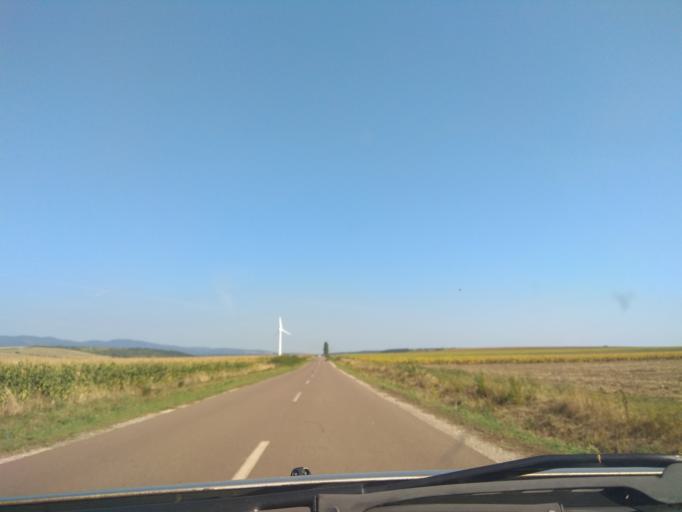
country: HU
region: Borsod-Abauj-Zemplen
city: Emod
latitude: 47.9620
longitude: 20.8032
